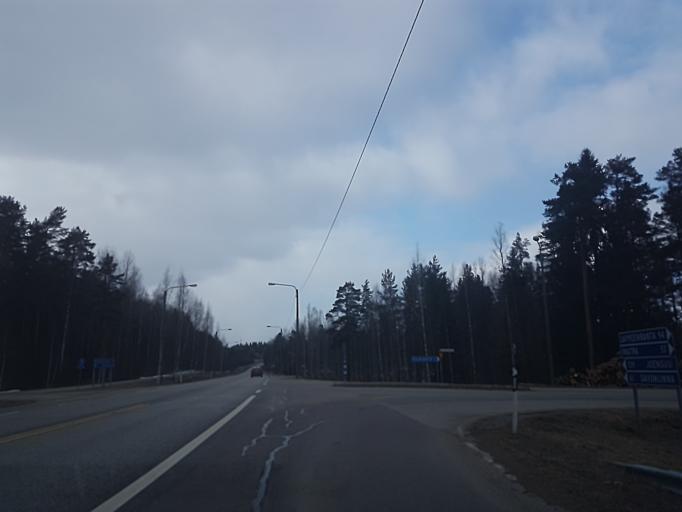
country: FI
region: South Karelia
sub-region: Imatra
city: Parikkala
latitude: 61.5305
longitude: 29.5176
